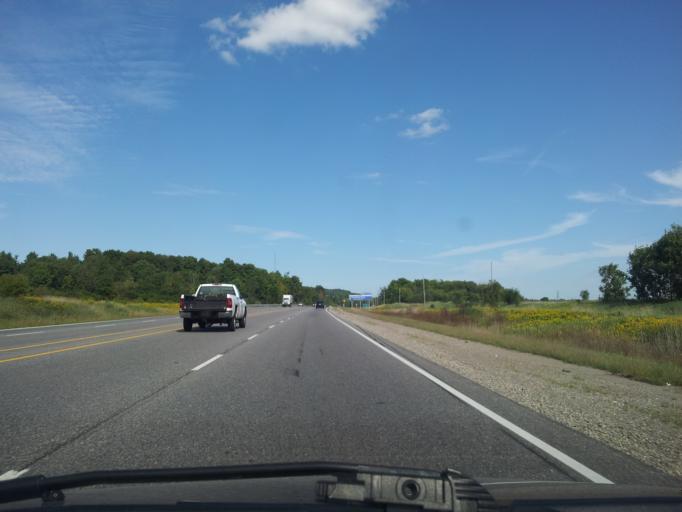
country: CA
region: Ontario
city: Kitchener
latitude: 43.3898
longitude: -80.6726
